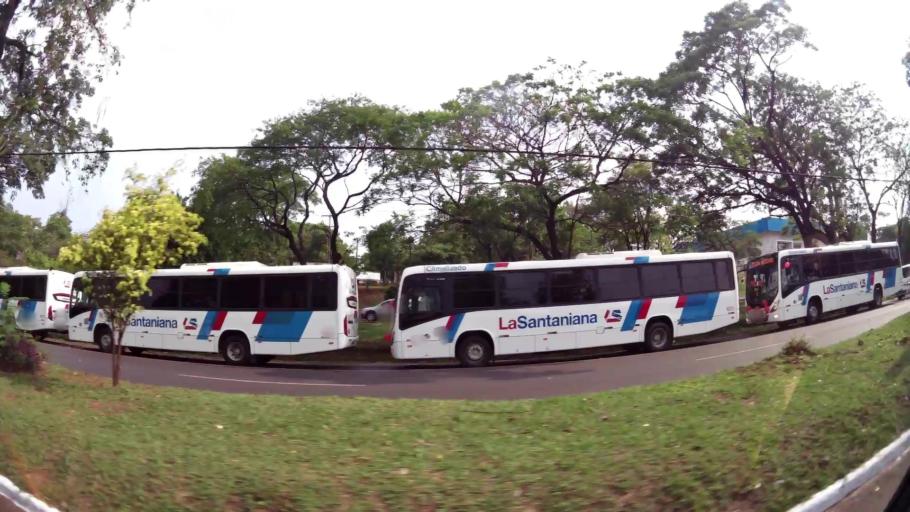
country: PY
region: Alto Parana
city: Ciudad del Este
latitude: -25.5091
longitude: -54.6319
